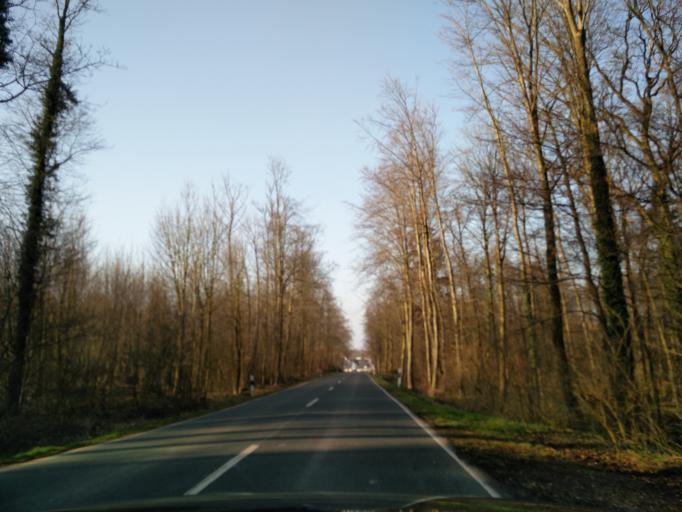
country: DE
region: North Rhine-Westphalia
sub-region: Regierungsbezirk Detmold
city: Paderborn
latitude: 51.6762
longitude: 8.6972
